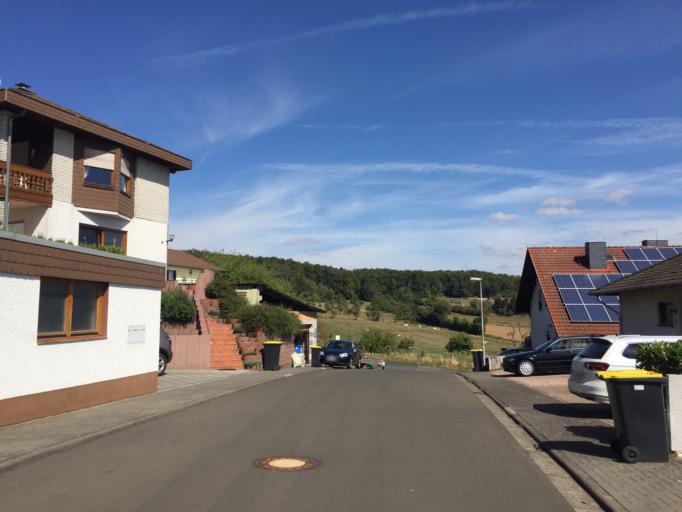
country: DE
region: Hesse
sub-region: Regierungsbezirk Giessen
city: Reiskirchen
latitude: 50.5988
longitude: 8.8819
